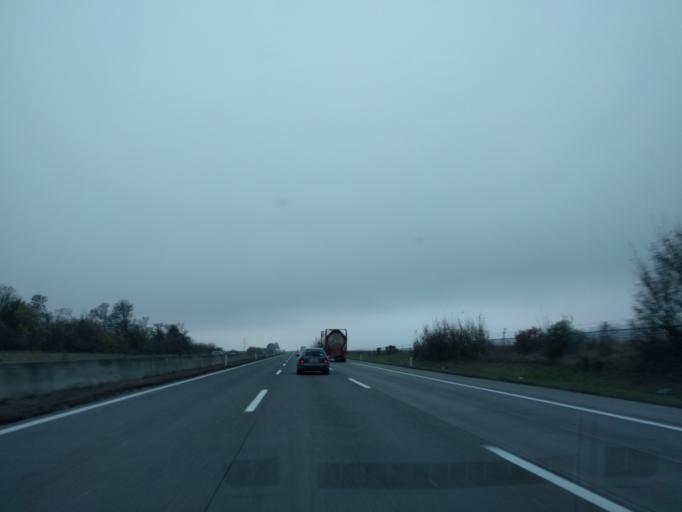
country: AT
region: Lower Austria
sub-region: Politischer Bezirk Sankt Polten
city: Haunoldstein
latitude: 48.1818
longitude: 15.4479
